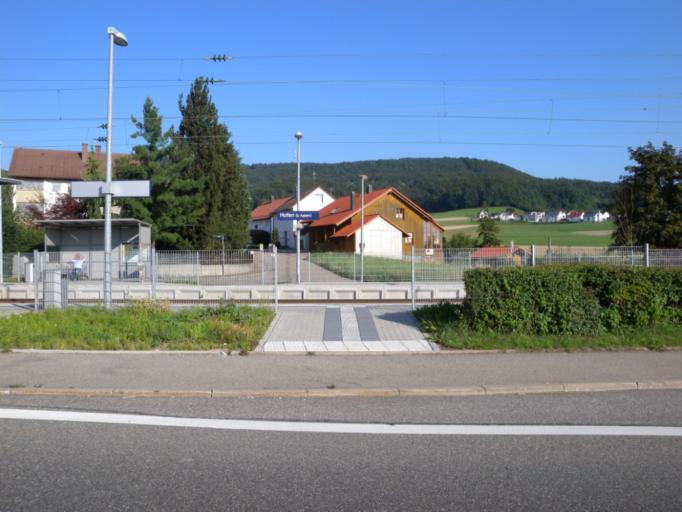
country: DE
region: Baden-Wuerttemberg
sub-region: Regierungsbezirk Stuttgart
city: Huttlingen
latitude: 48.8726
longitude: 10.1142
